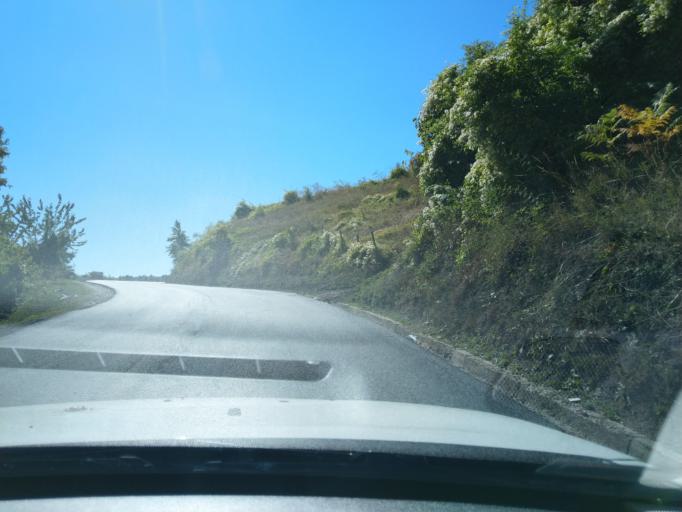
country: RS
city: Sokolovica
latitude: 43.2583
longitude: 20.2315
